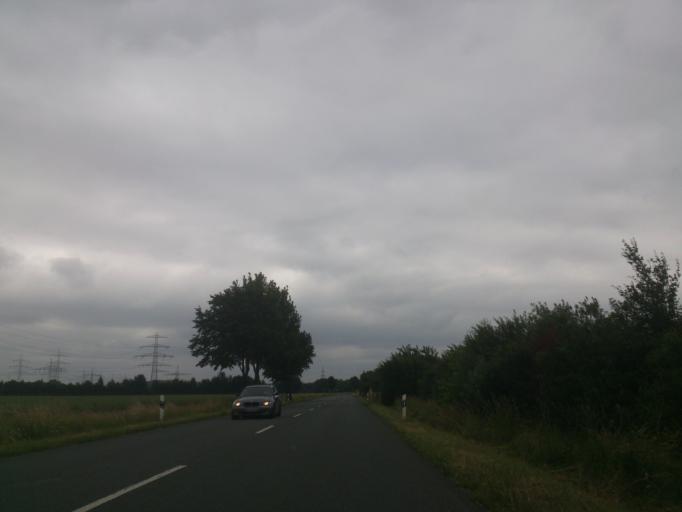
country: DE
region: North Rhine-Westphalia
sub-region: Regierungsbezirk Detmold
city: Paderborn
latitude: 51.7112
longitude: 8.6975
